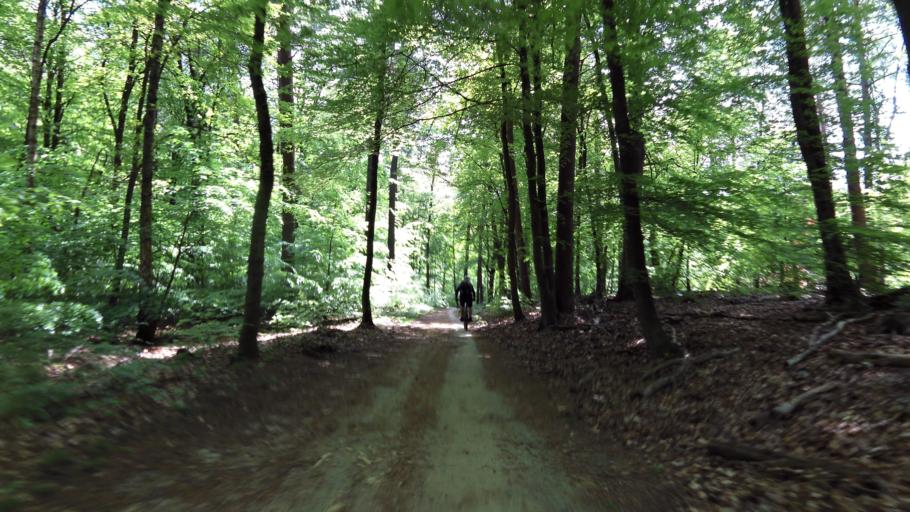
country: NL
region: Gelderland
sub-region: Gemeente Rheden
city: De Steeg
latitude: 52.0201
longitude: 6.0447
